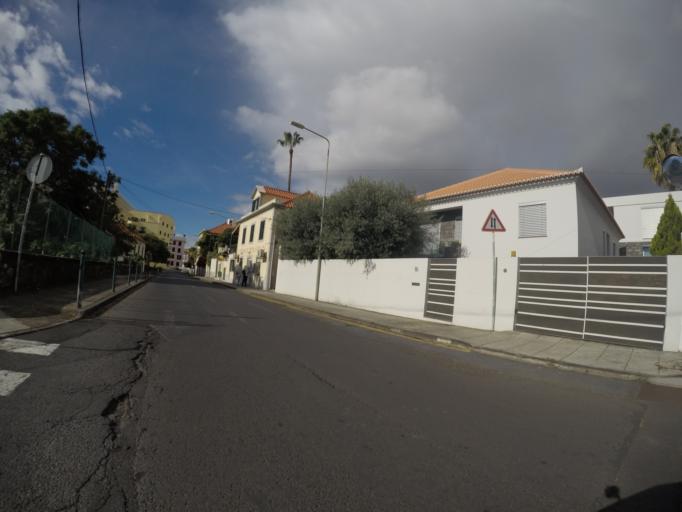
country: PT
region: Madeira
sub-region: Funchal
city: Funchal
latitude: 32.6404
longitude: -16.9278
